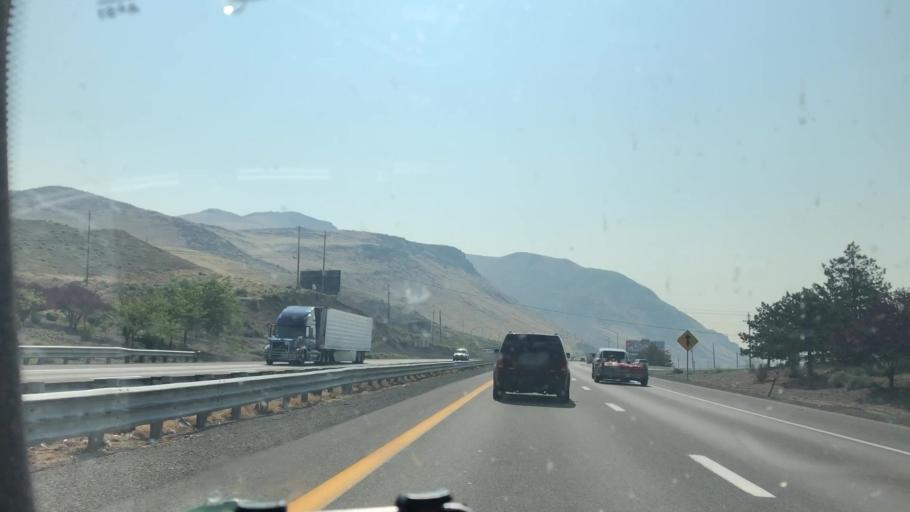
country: US
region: Nevada
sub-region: Washoe County
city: Sparks
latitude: 39.5261
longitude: -119.7000
